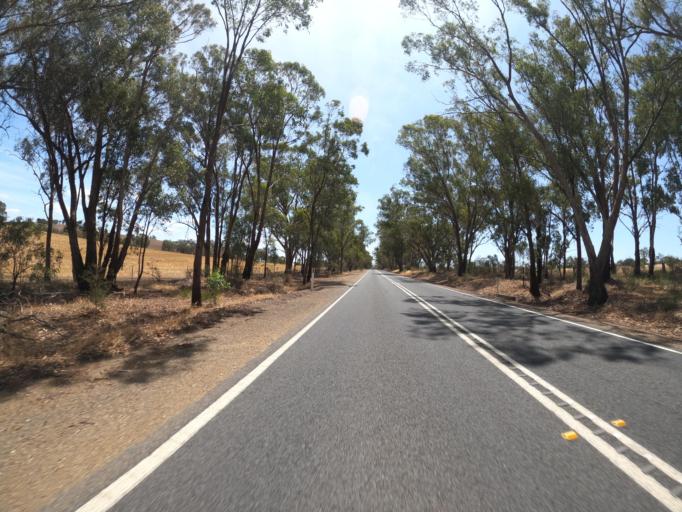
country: AU
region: Victoria
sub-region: Benalla
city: Benalla
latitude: -36.3746
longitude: 145.9741
